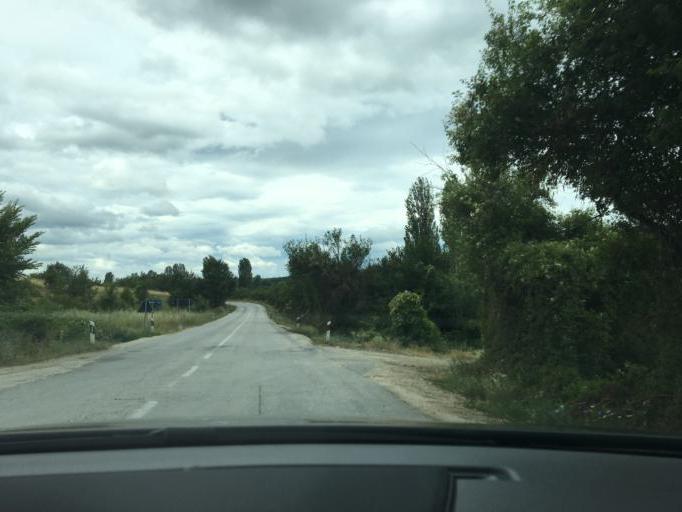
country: MK
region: Kriva Palanka
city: Kriva Palanka
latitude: 42.1786
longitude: 22.2643
